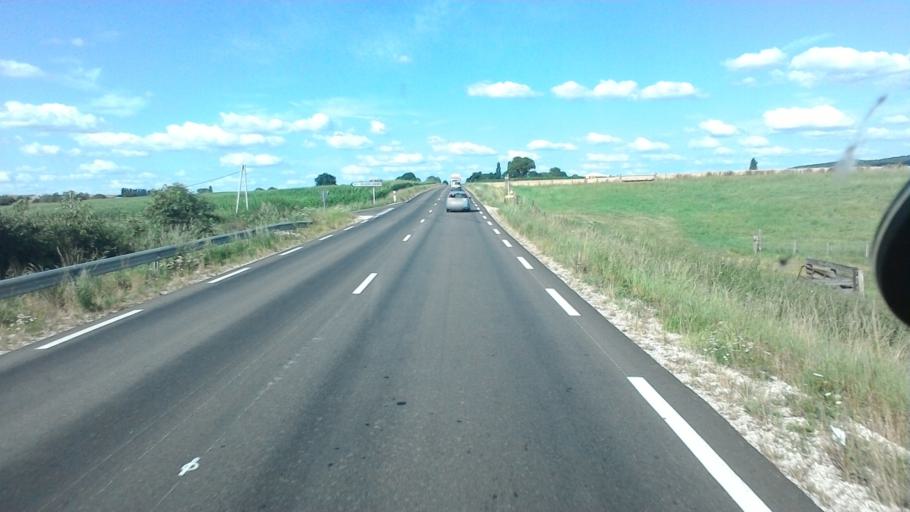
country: FR
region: Franche-Comte
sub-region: Departement de la Haute-Saone
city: Gy
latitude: 47.4358
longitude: 5.8677
